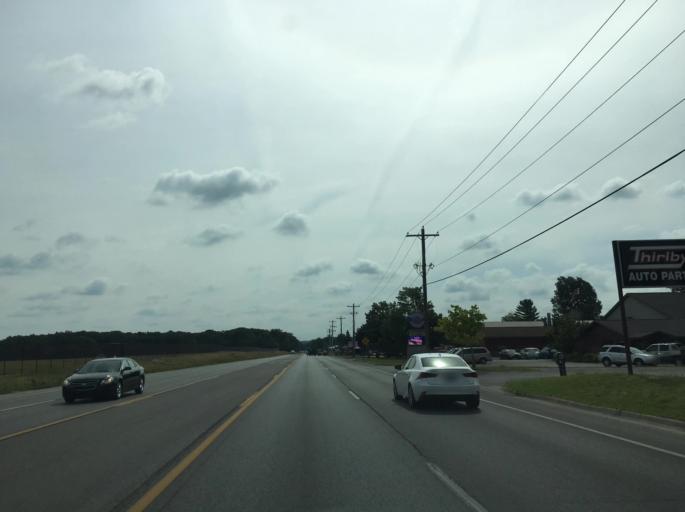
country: US
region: Michigan
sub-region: Grand Traverse County
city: Traverse City
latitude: 44.7333
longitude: -85.5924
